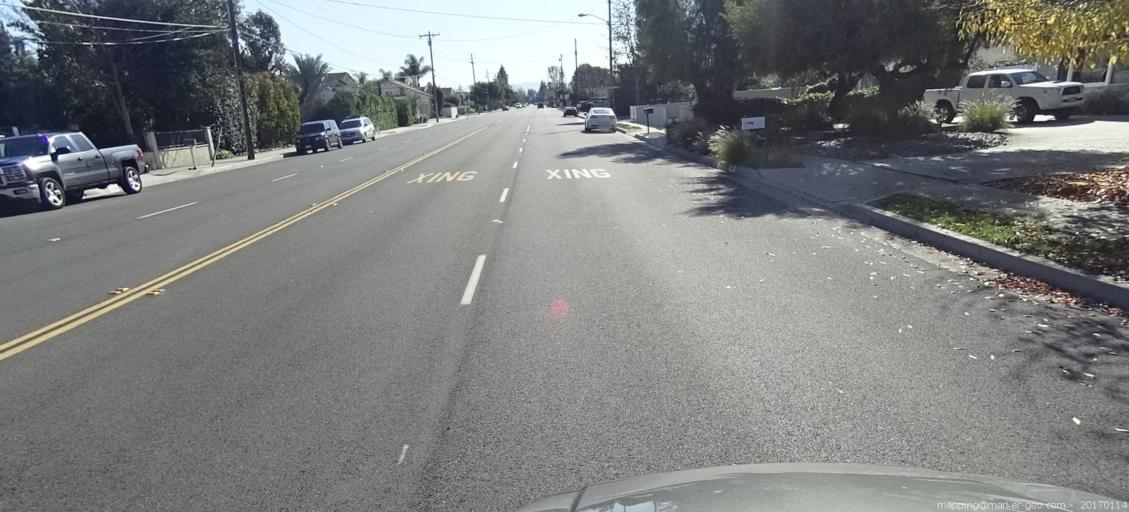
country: US
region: California
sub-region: Orange County
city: Tustin
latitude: 33.7552
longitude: -117.8144
